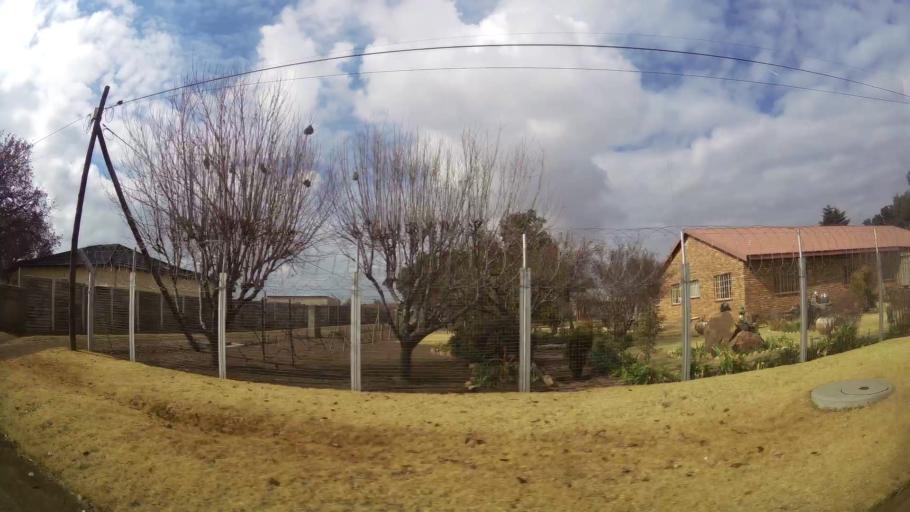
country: ZA
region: Gauteng
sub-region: Sedibeng District Municipality
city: Meyerton
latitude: -26.6051
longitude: 28.0526
